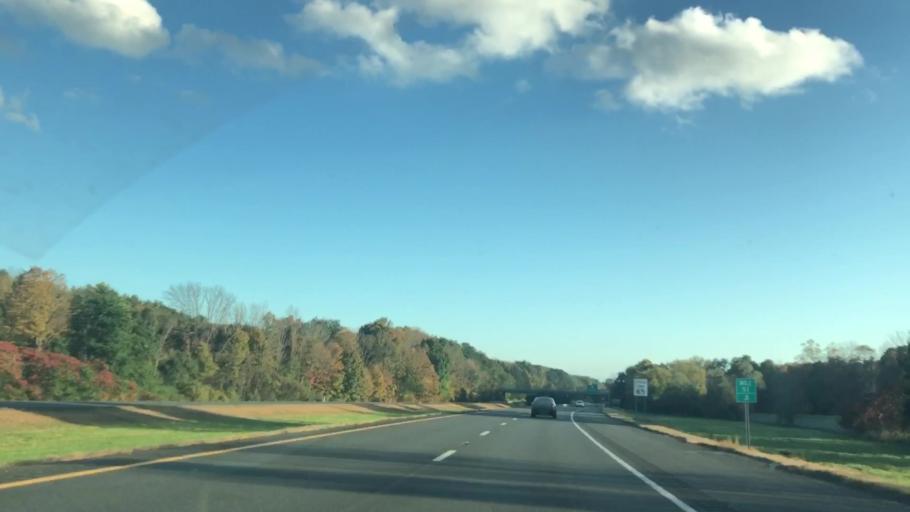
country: US
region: Massachusetts
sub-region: Franklin County
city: Bernardston
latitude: 42.6913
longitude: -72.5444
